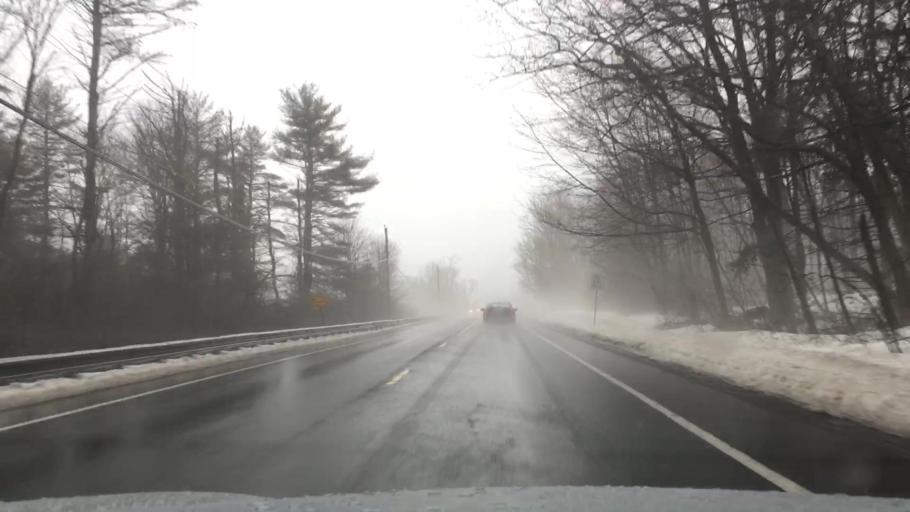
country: US
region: Massachusetts
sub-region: Franklin County
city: Orange
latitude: 42.5398
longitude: -72.3022
